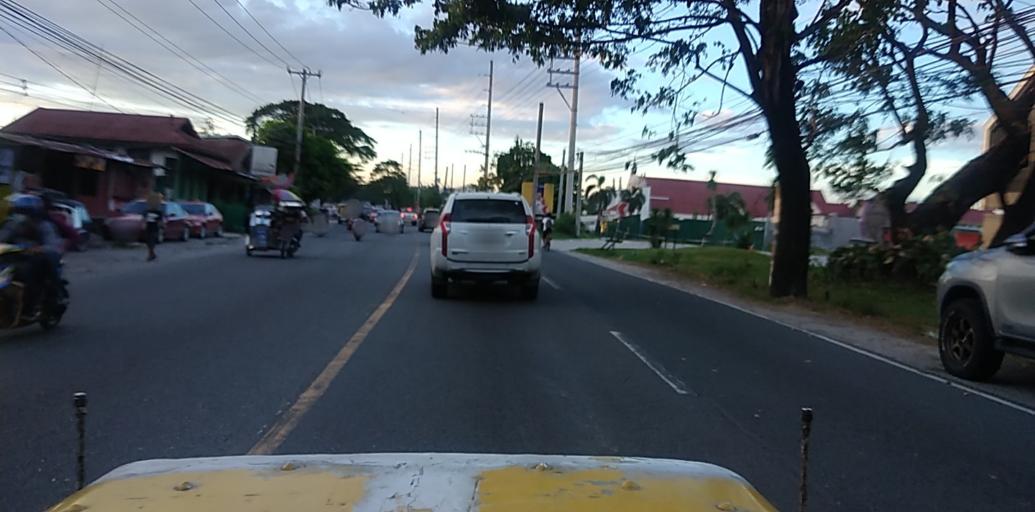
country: PH
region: Central Luzon
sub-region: Province of Pampanga
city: Telabastagan
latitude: 15.1166
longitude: 120.6068
